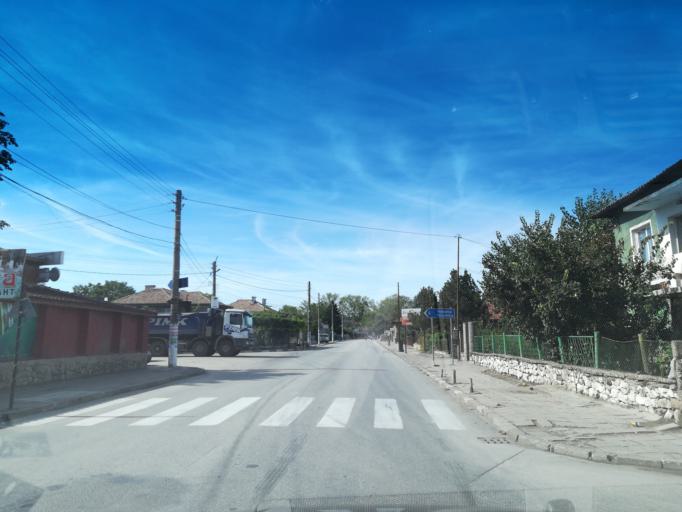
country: BG
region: Plovdiv
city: Stamboliyski
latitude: 42.1189
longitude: 24.5611
